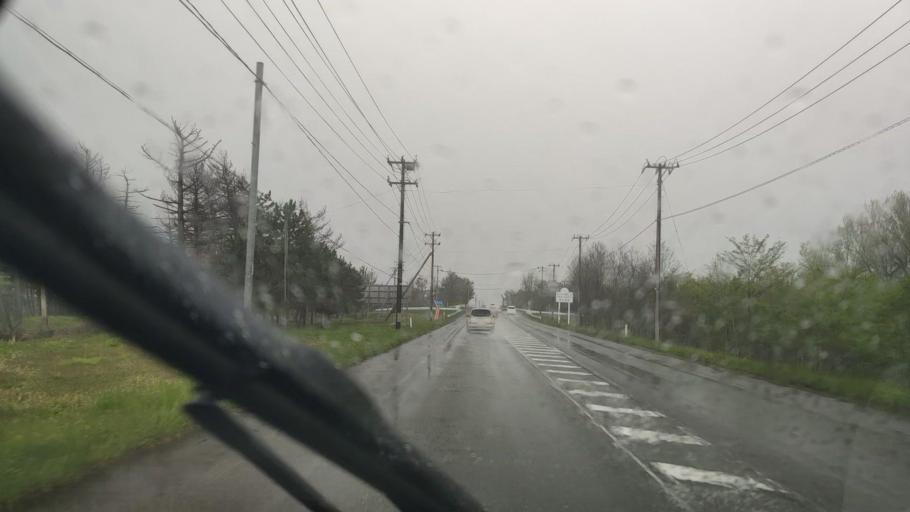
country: JP
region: Akita
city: Tenno
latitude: 39.9460
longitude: 139.9458
